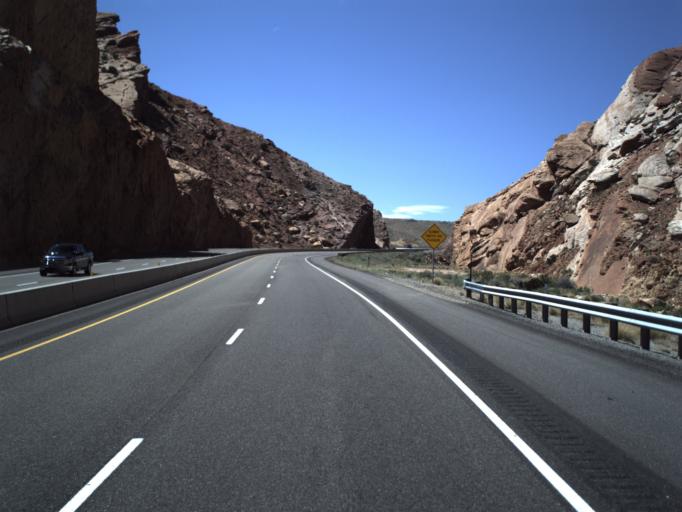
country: US
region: Utah
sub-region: Carbon County
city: East Carbon City
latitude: 38.9223
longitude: -110.4417
